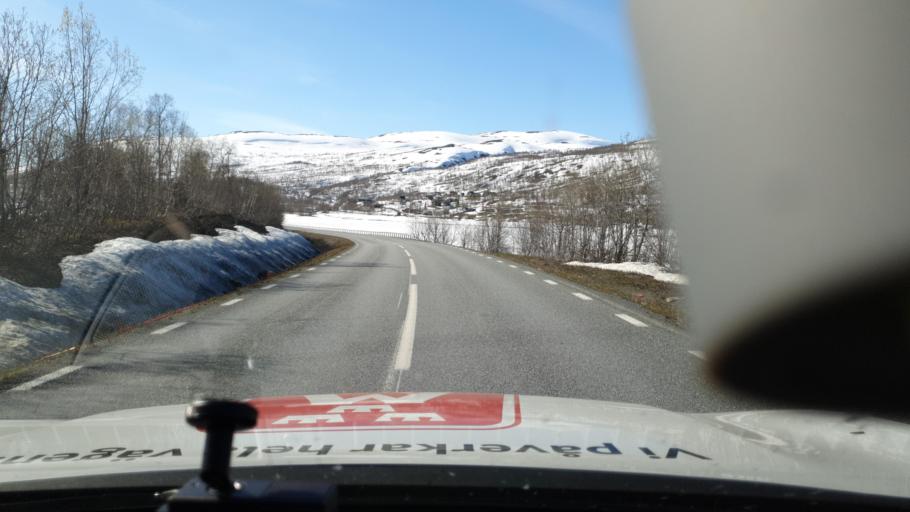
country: NO
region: Nordland
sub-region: Rana
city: Mo i Rana
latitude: 66.1183
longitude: 14.8044
